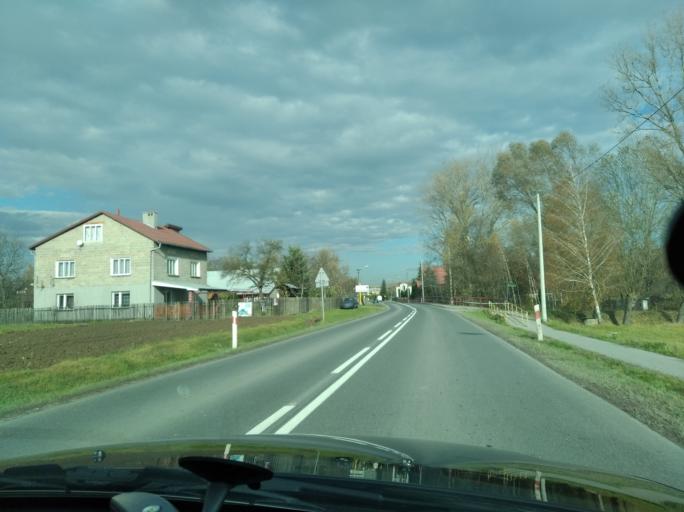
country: PL
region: Subcarpathian Voivodeship
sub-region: Powiat ropczycko-sedziszowski
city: Ostrow
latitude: 50.0947
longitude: 21.5935
